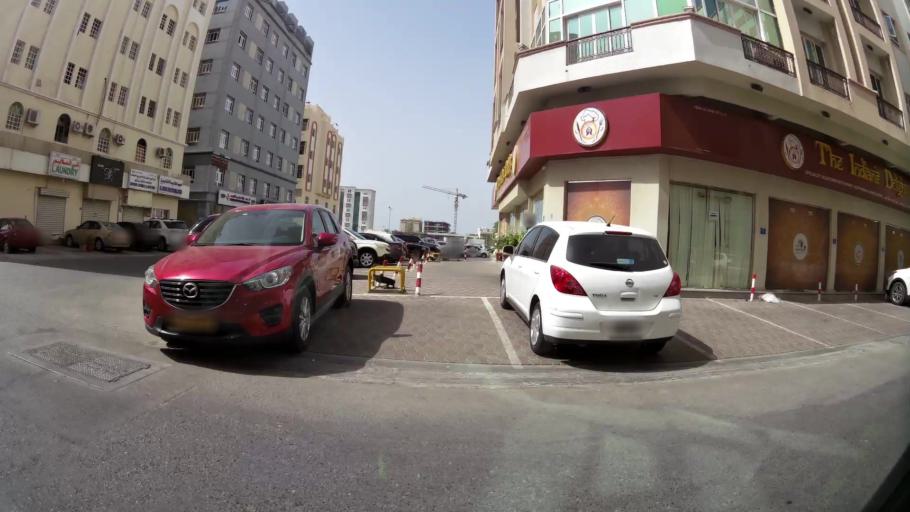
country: OM
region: Muhafazat Masqat
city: Bawshar
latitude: 23.5812
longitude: 58.3965
